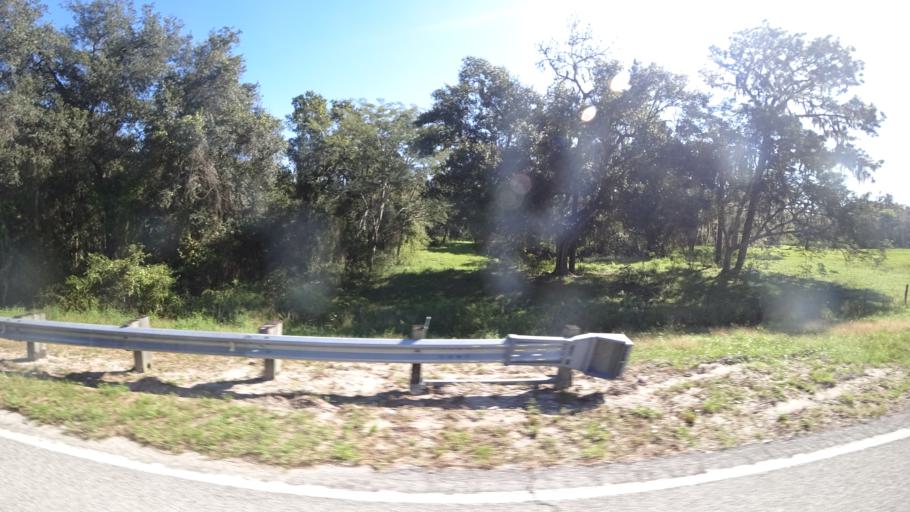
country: US
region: Florida
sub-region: Hillsborough County
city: Wimauma
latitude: 27.6490
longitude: -82.2943
